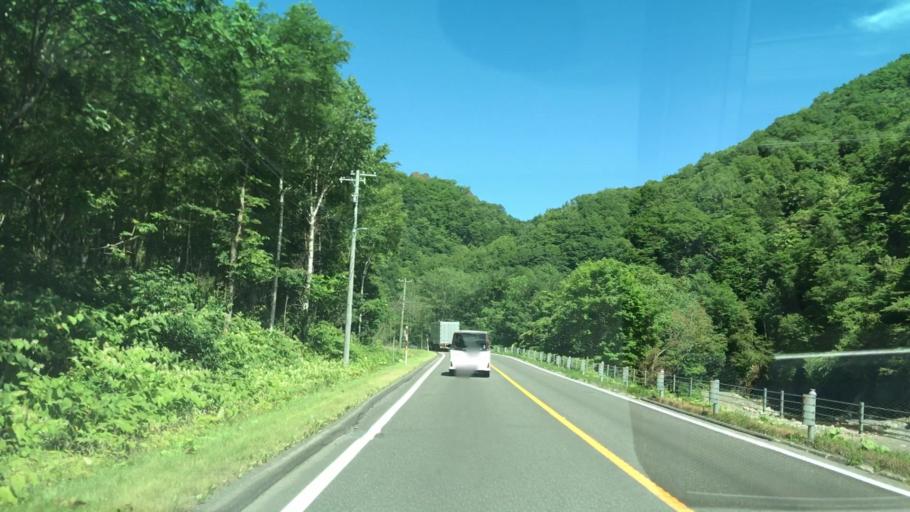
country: JP
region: Hokkaido
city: Shimo-furano
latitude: 42.9146
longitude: 142.5873
